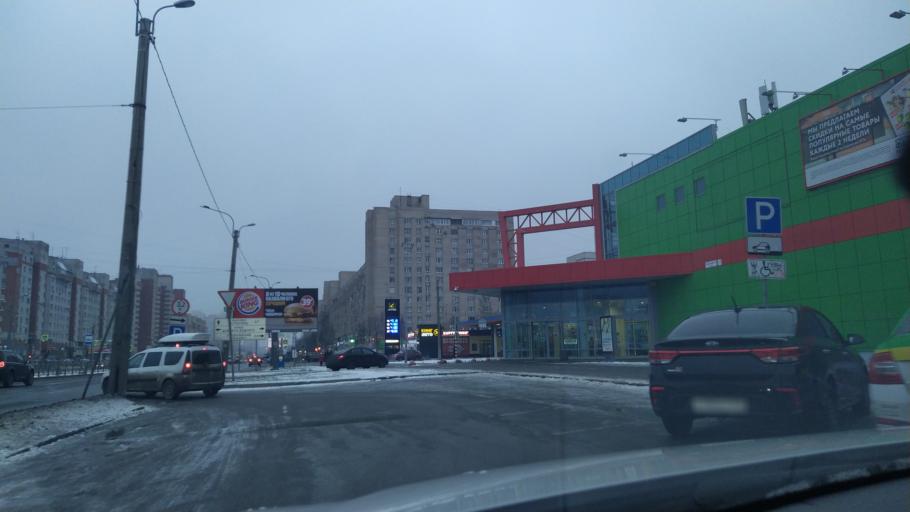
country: RU
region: St.-Petersburg
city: Grazhdanka
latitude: 60.0421
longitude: 30.3890
